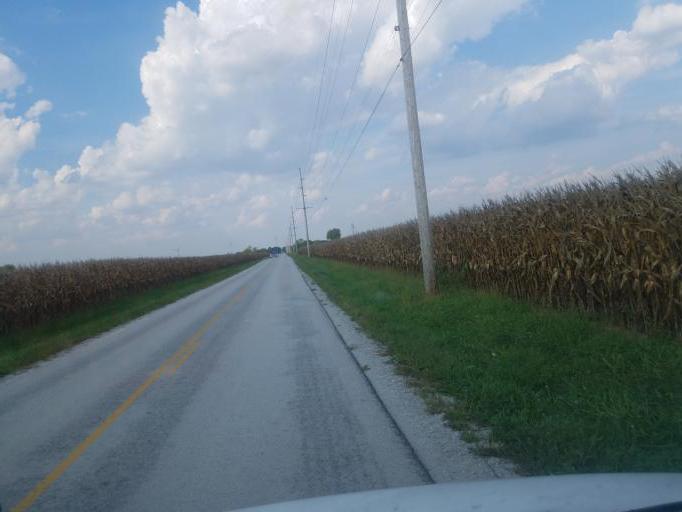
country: US
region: Ohio
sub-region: Hardin County
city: Kenton
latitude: 40.7662
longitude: -83.6523
